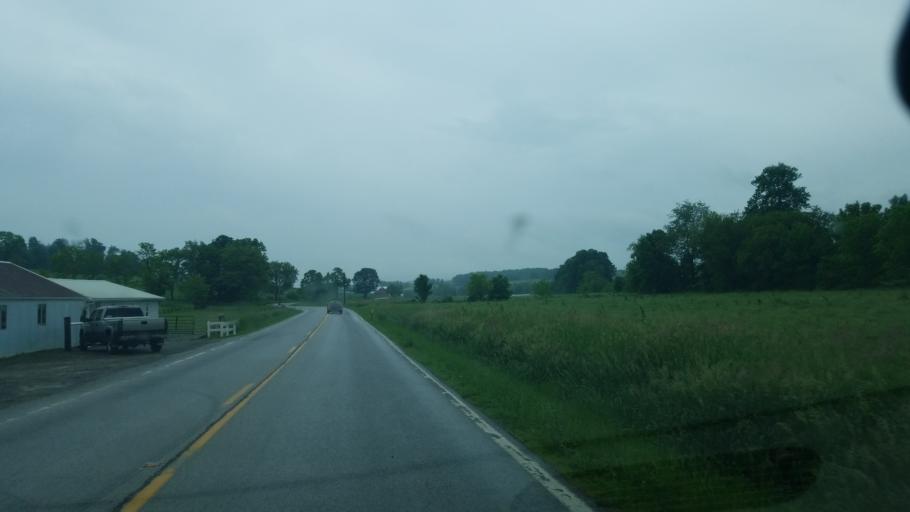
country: US
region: Ohio
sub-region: Tuscarawas County
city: Sugarcreek
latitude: 40.4757
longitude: -81.7147
